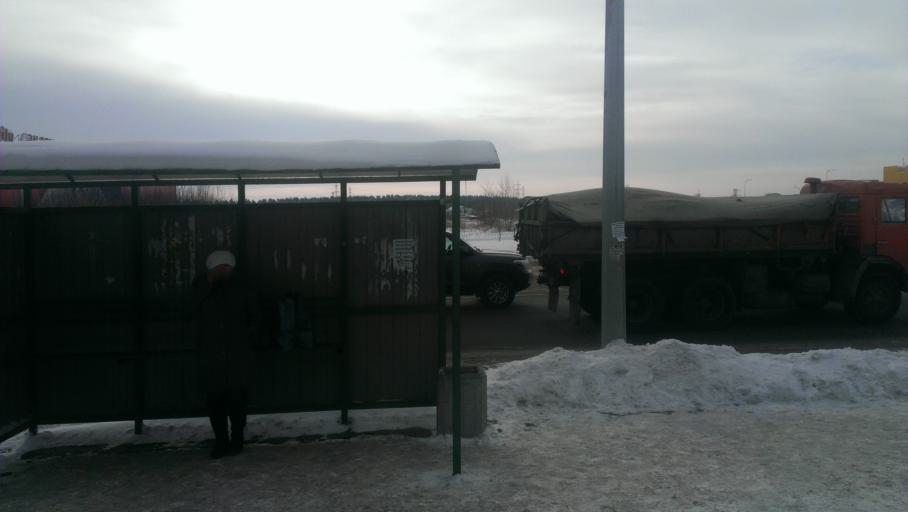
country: RU
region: Altai Krai
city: Novosilikatnyy
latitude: 53.3278
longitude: 83.6888
